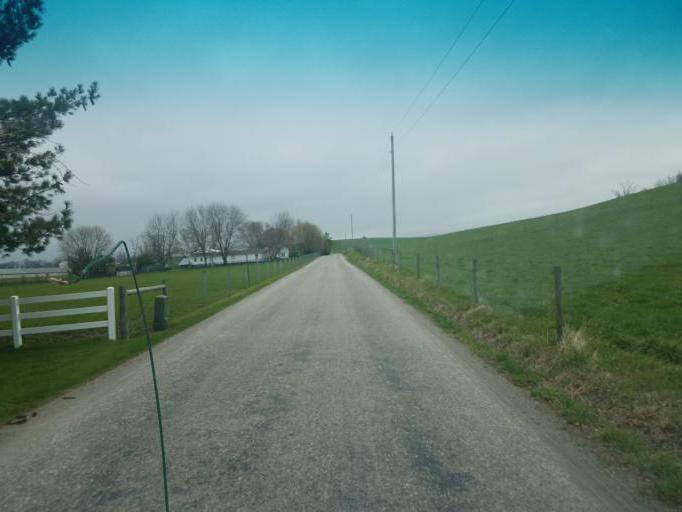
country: US
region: Ohio
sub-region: Tuscarawas County
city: Sugarcreek
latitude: 40.6149
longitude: -81.7311
